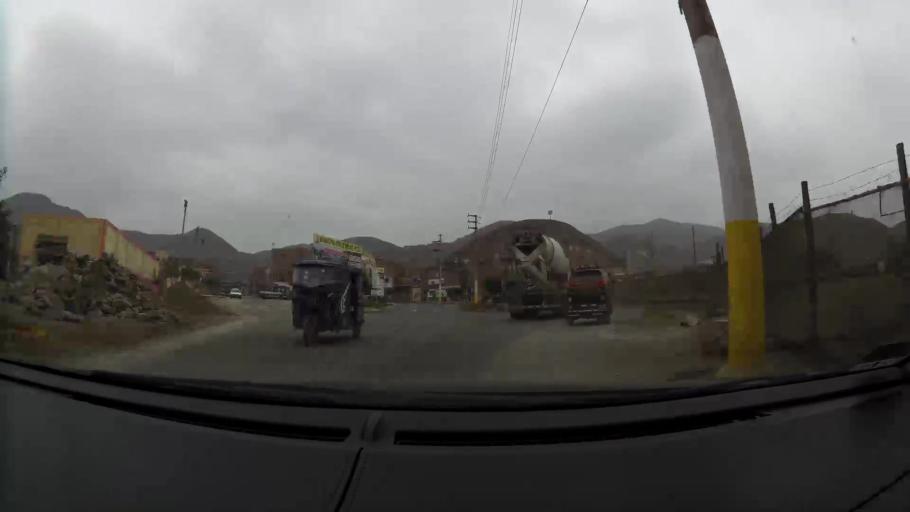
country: PE
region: Lima
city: Ventanilla
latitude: -11.9206
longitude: -77.0831
